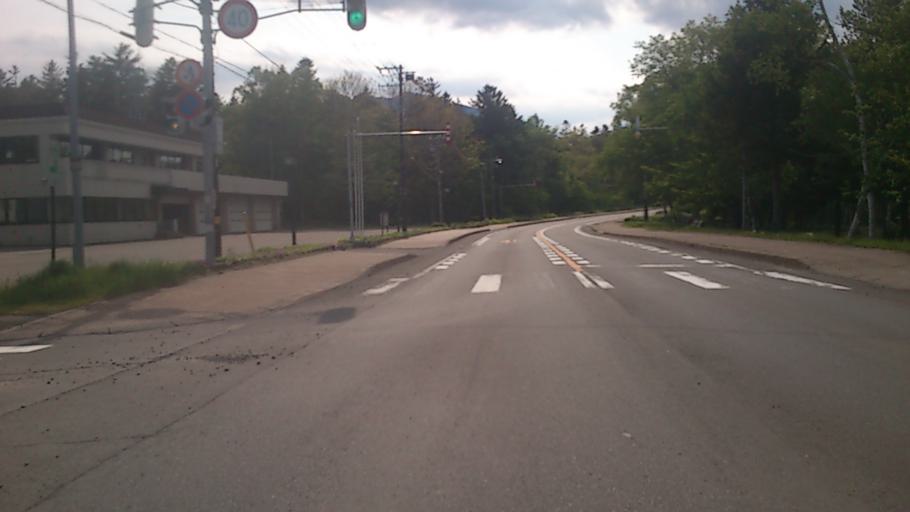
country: JP
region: Hokkaido
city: Bihoro
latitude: 43.4312
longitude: 144.0935
